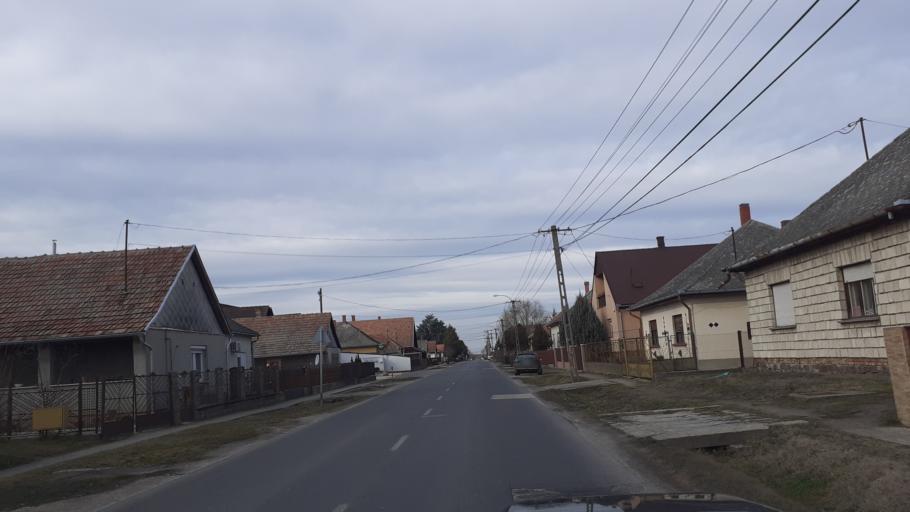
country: HU
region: Fejer
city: Sarbogard
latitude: 46.8997
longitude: 18.6037
